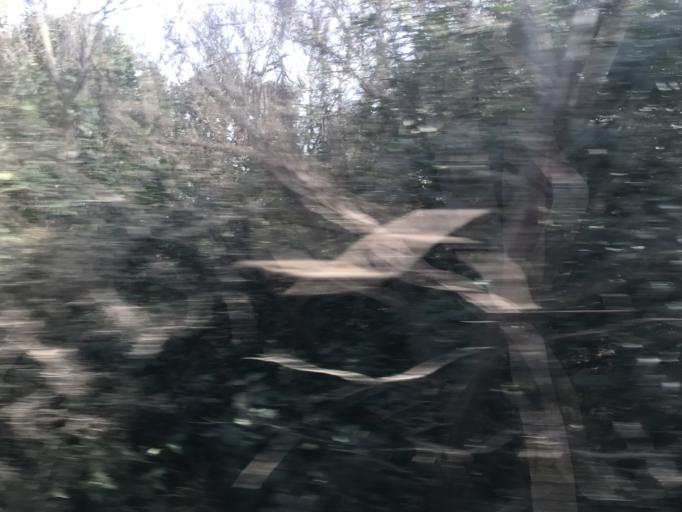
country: AR
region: Cordoba
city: Laguna Larga
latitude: -31.7669
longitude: -63.8118
